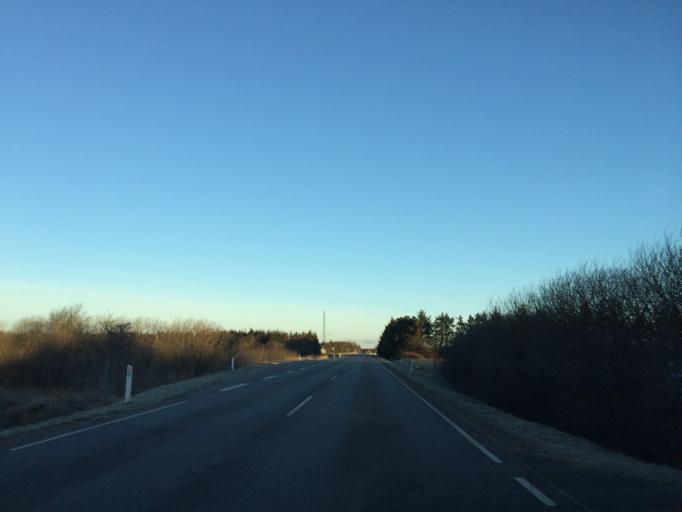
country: DK
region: Central Jutland
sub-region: Holstebro Kommune
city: Ulfborg
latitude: 56.3970
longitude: 8.3189
